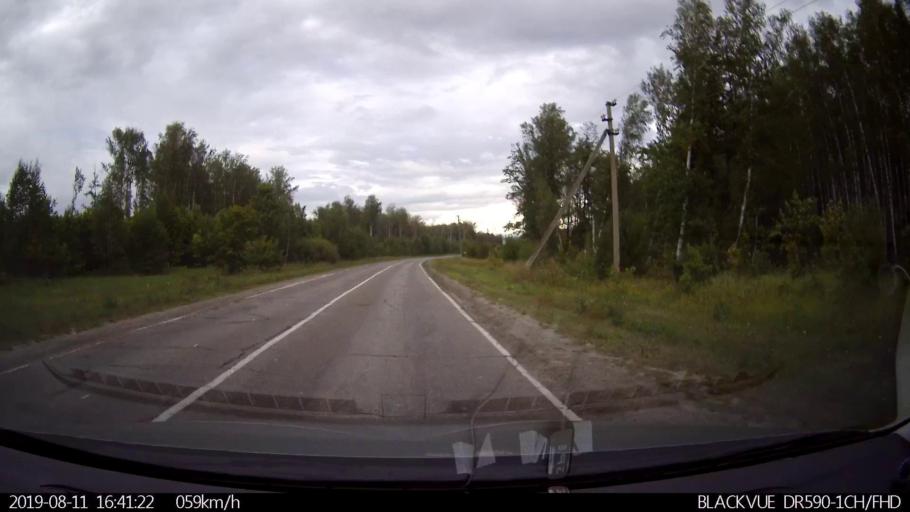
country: RU
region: Ulyanovsk
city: Mayna
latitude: 54.1528
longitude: 47.6523
